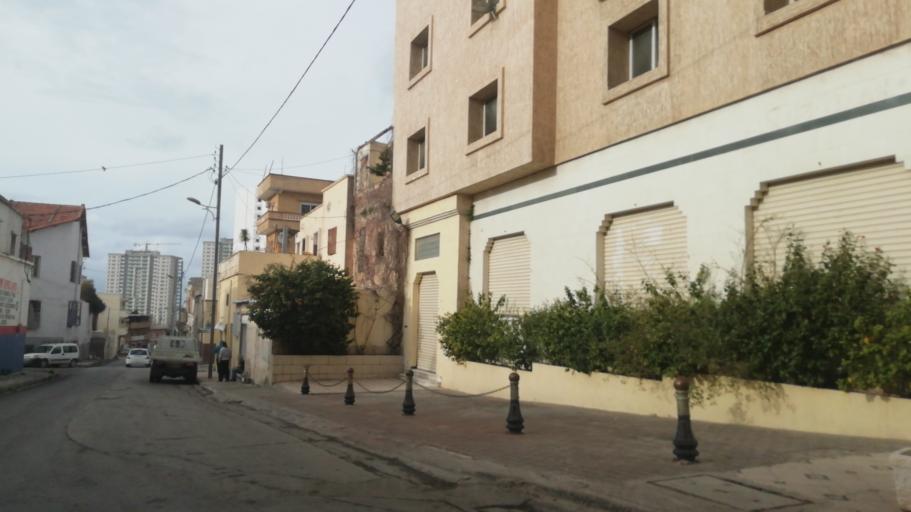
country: DZ
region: Oran
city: Oran
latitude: 35.7022
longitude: -0.6234
